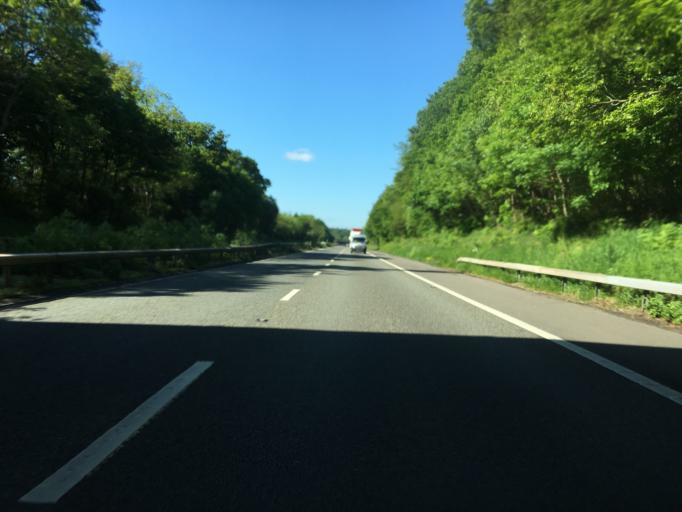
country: GB
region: England
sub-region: Gloucestershire
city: Newent
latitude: 51.9540
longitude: -2.4485
